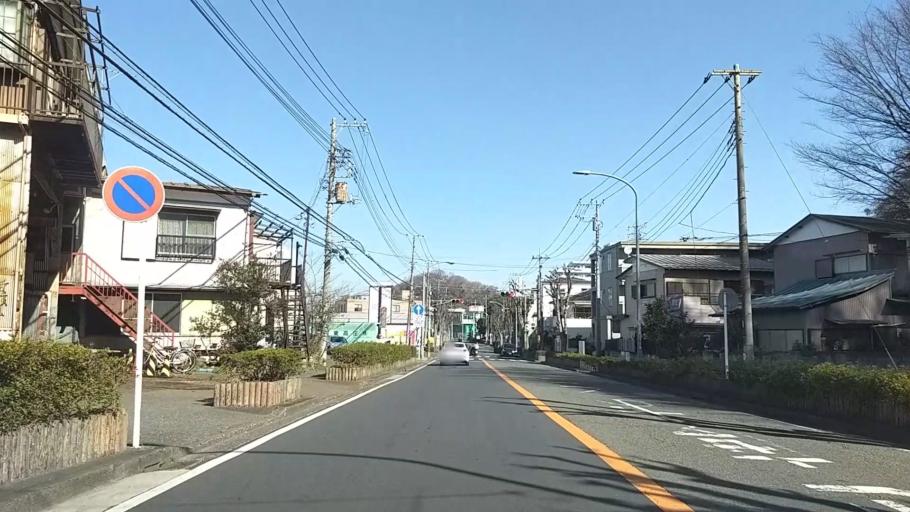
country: JP
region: Kanagawa
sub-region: Kawasaki-shi
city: Kawasaki
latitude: 35.5217
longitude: 139.6510
